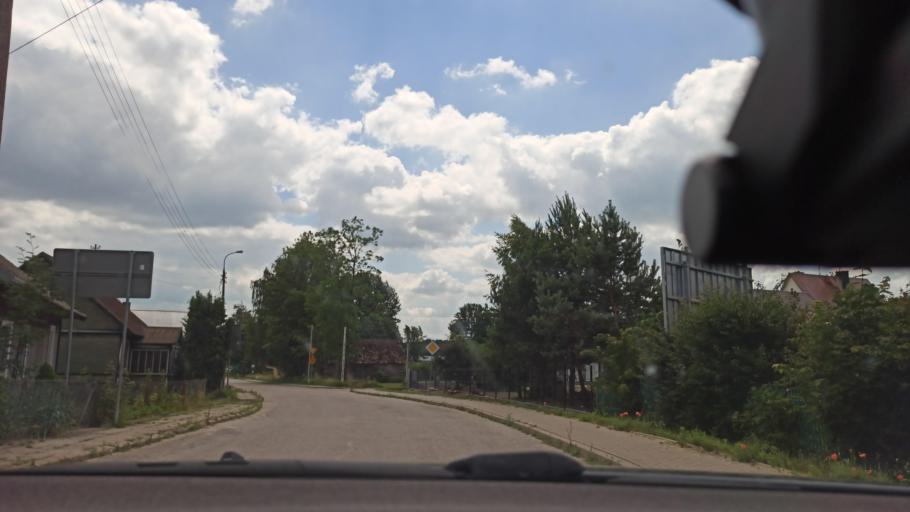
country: PL
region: Podlasie
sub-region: Powiat bialostocki
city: Turosn Koscielna
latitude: 53.0196
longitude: 23.0030
